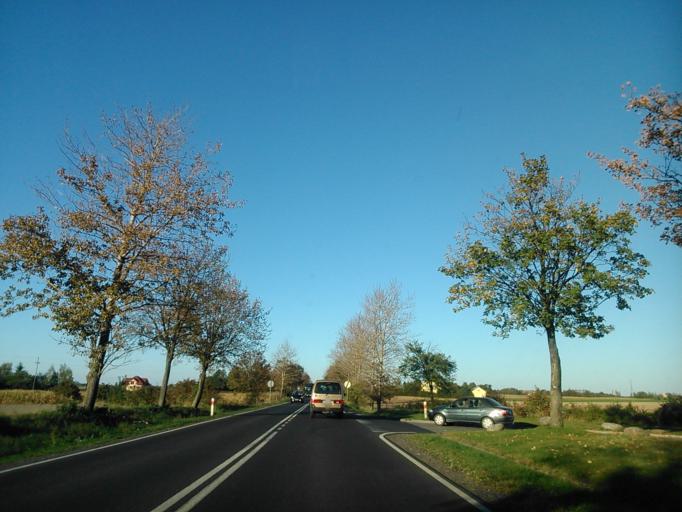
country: PL
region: Kujawsko-Pomorskie
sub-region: Powiat torunski
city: Lubicz Gorny
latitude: 53.0922
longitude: 18.7759
